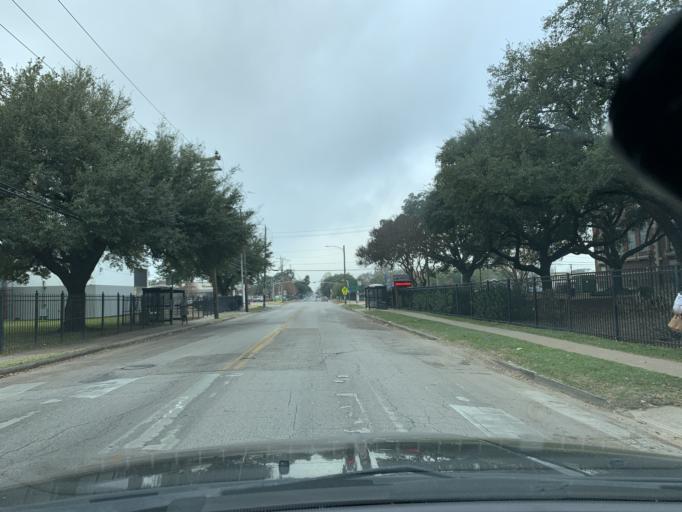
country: US
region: Texas
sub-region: Harris County
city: Houston
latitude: 29.7828
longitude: -95.3583
